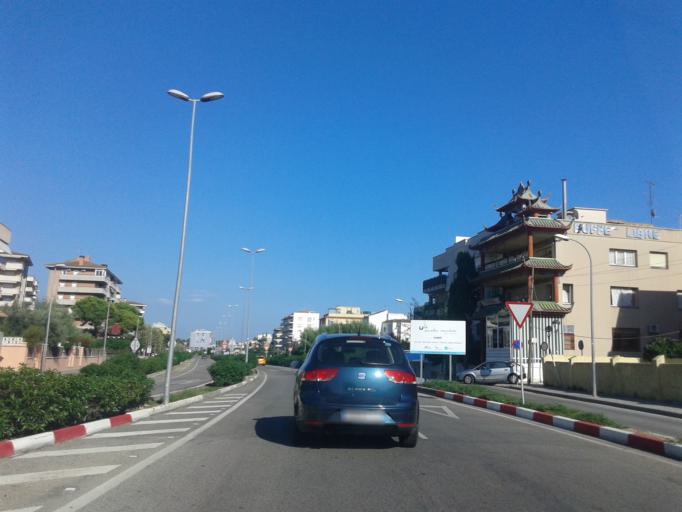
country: ES
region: Catalonia
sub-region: Provincia de Tarragona
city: Cunit
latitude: 41.1944
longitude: 1.6149
